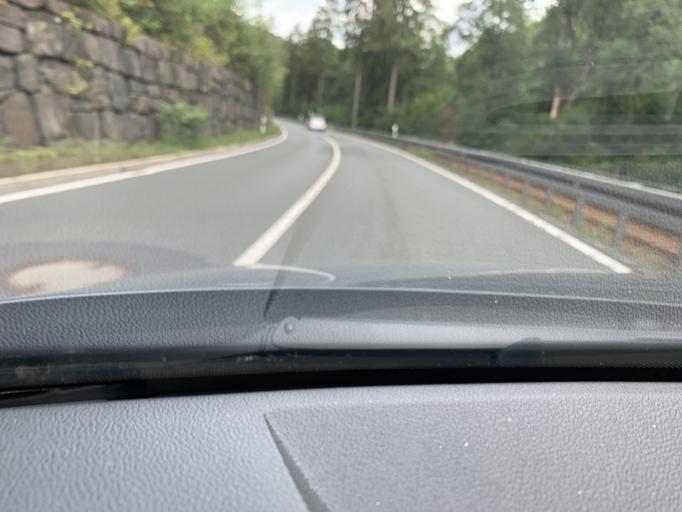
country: DE
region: Thuringia
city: Steinach
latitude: 50.4119
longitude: 11.1801
